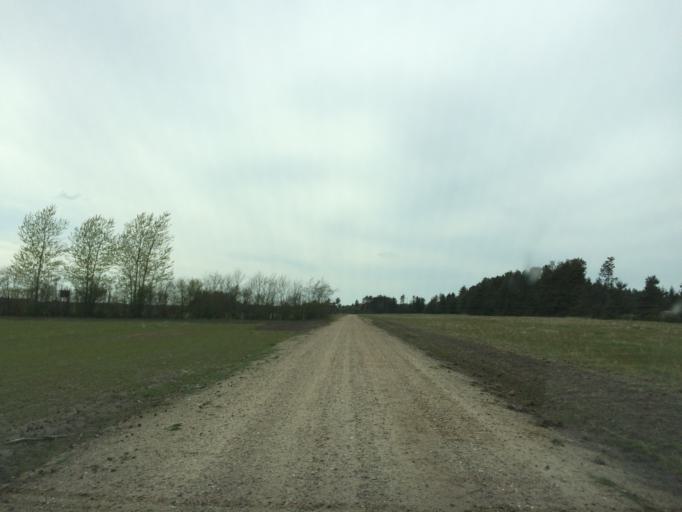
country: DK
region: Central Jutland
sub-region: Holstebro Kommune
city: Ulfborg
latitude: 56.2451
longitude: 8.4432
